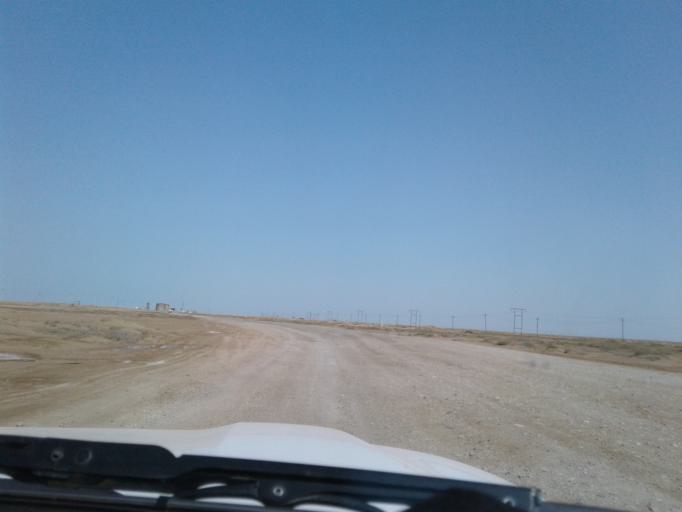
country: IR
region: Golestan
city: Gomishan
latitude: 37.7589
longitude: 53.9274
